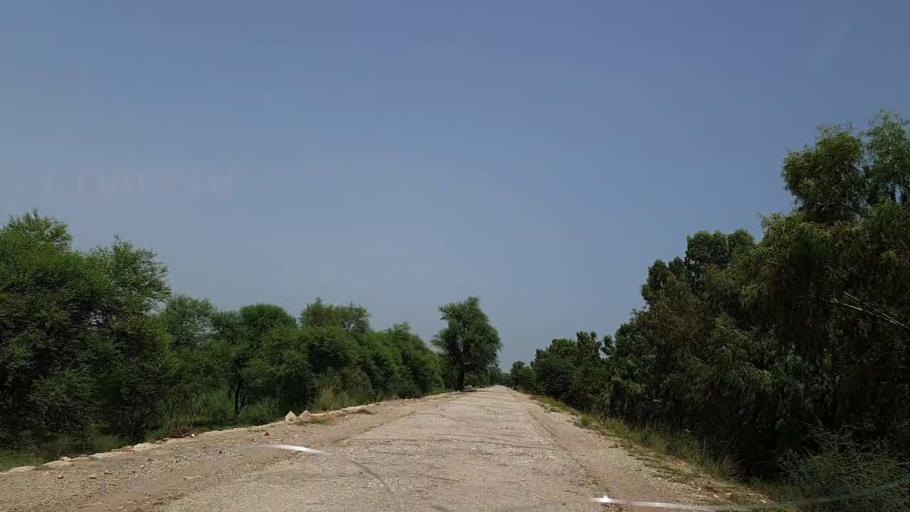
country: PK
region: Sindh
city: Tharu Shah
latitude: 27.0045
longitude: 68.0968
